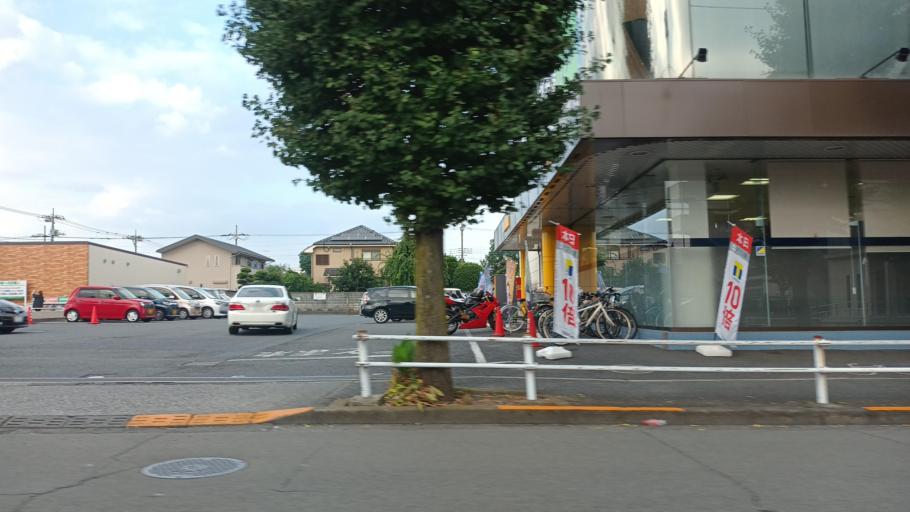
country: JP
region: Tokyo
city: Fussa
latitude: 35.7727
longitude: 139.3077
